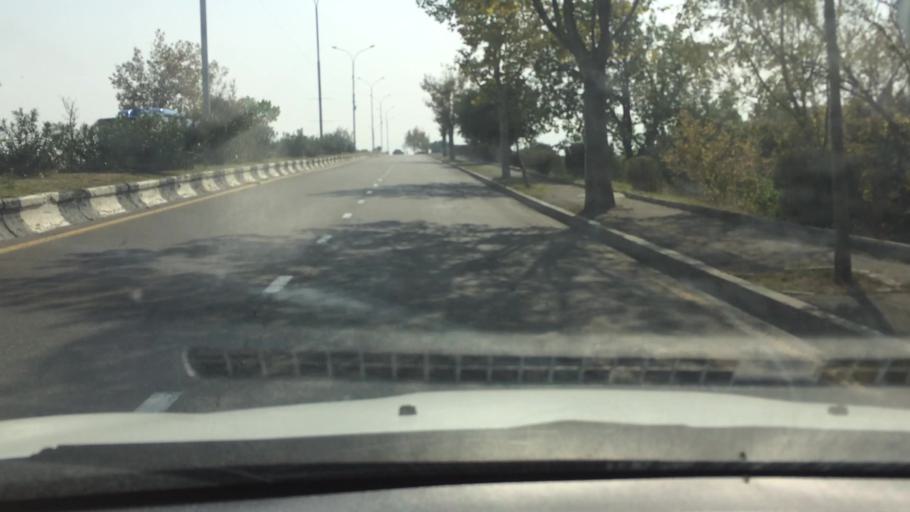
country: GE
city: Didi Lilo
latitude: 41.6880
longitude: 44.9530
